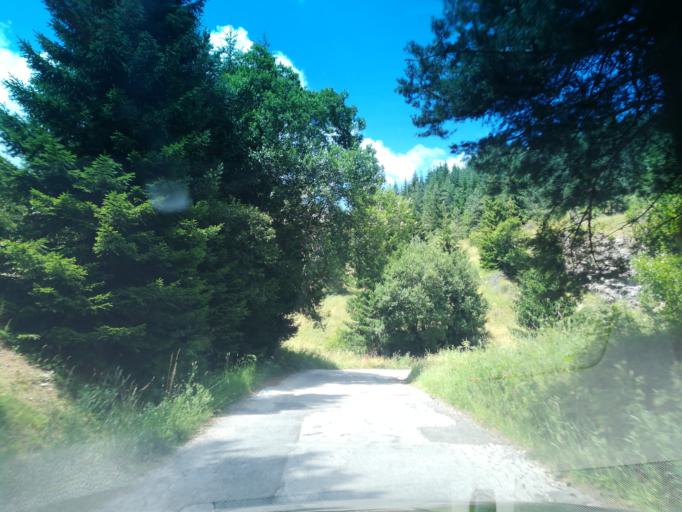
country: BG
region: Smolyan
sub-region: Obshtina Chepelare
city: Chepelare
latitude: 41.6792
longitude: 24.7697
